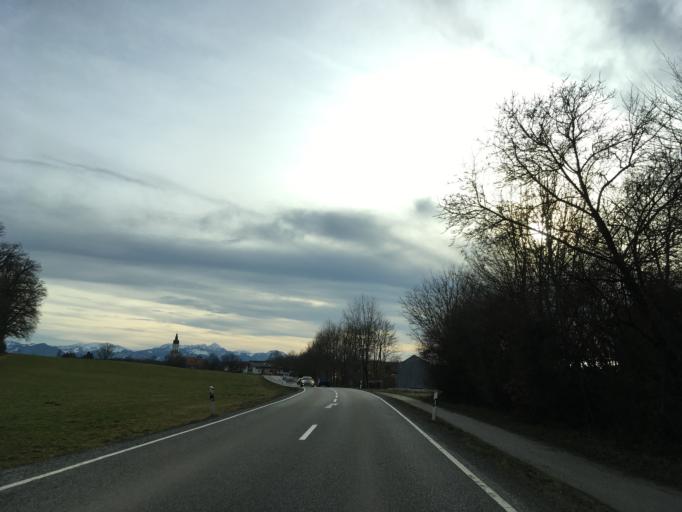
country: DE
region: Bavaria
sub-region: Upper Bavaria
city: Prutting
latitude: 47.9000
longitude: 12.2056
